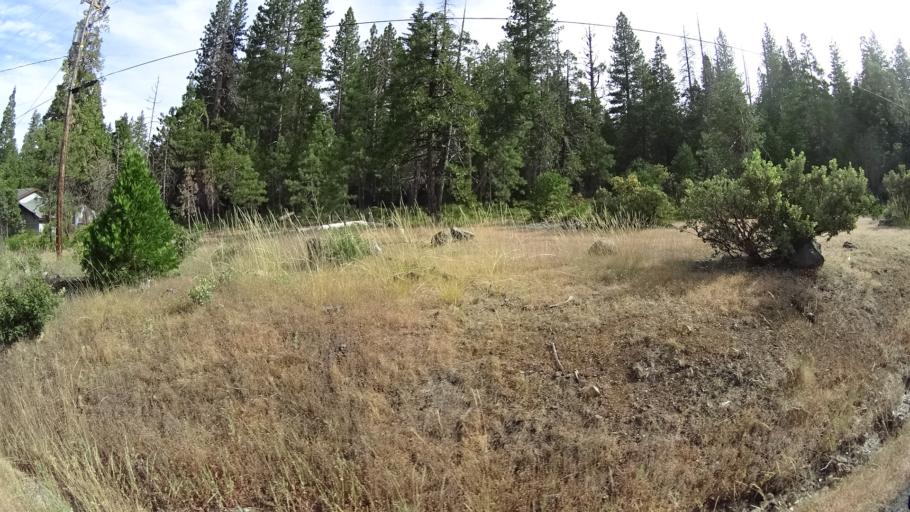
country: US
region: California
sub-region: Calaveras County
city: Arnold
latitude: 38.2670
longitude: -120.3259
